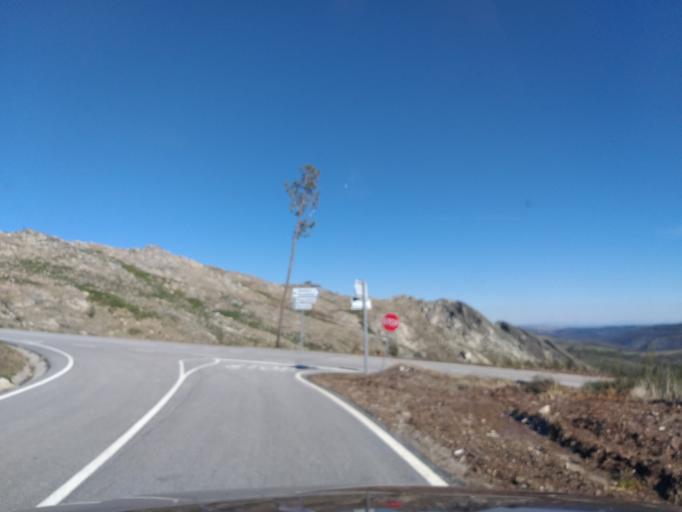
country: PT
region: Guarda
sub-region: Manteigas
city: Manteigas
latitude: 40.4767
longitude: -7.5076
